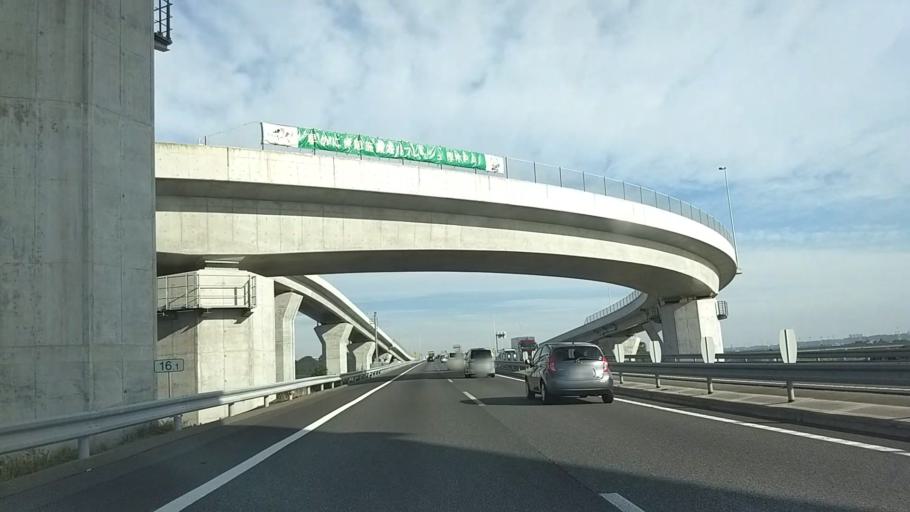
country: JP
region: Kanagawa
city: Zama
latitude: 35.4797
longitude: 139.3728
